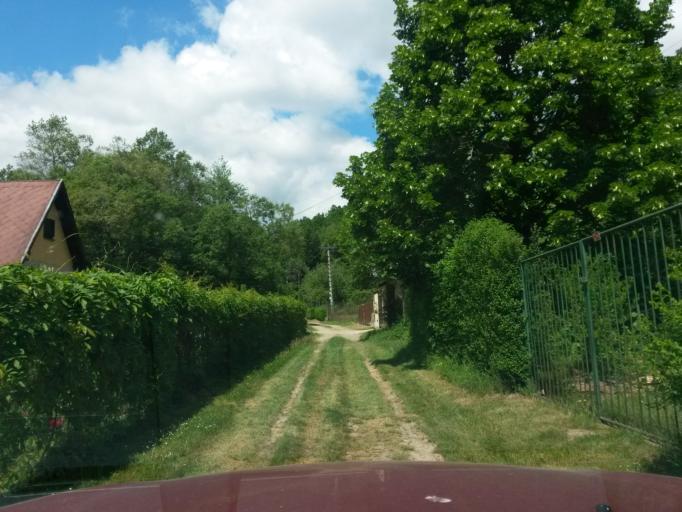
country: SK
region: Kosicky
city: Kosice
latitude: 48.7368
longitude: 21.1193
